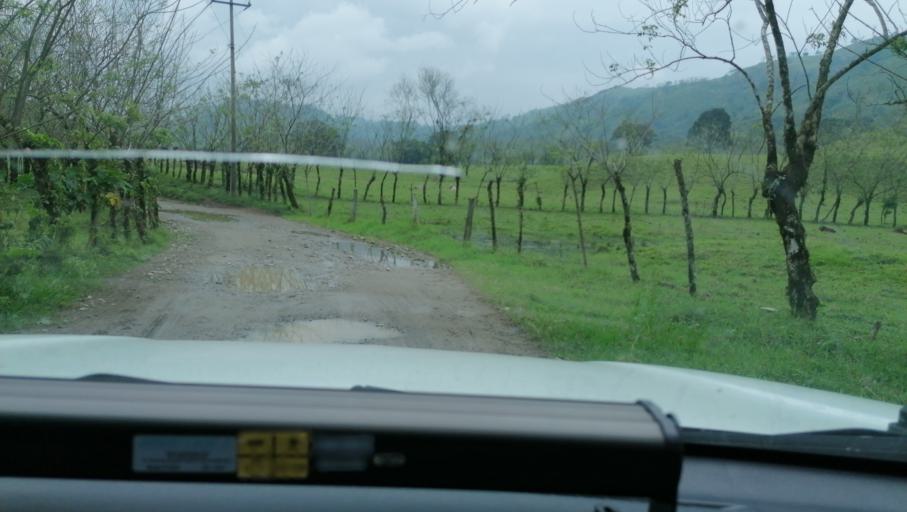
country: MX
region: Chiapas
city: Ixtacomitan
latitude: 17.3581
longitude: -93.1700
